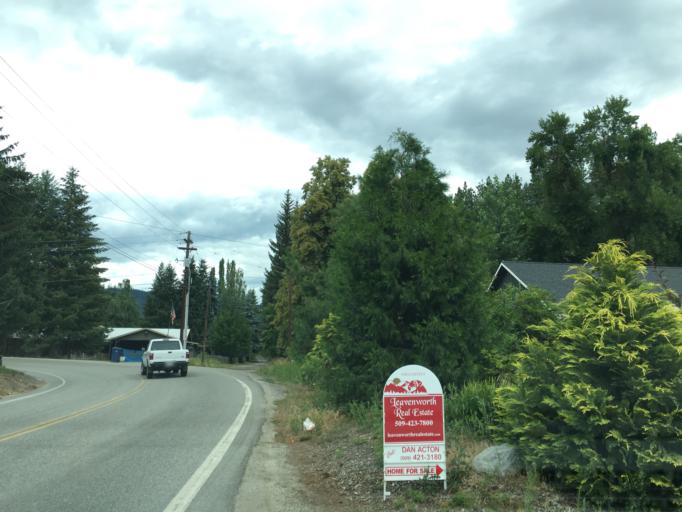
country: US
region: Washington
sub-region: Chelan County
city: Leavenworth
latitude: 47.5856
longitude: -120.6580
